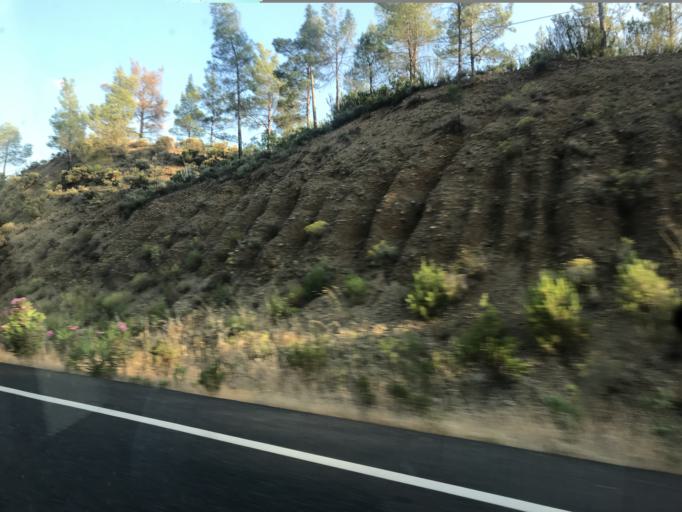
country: TR
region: Mugla
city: Ula
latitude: 37.0107
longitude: 28.5360
